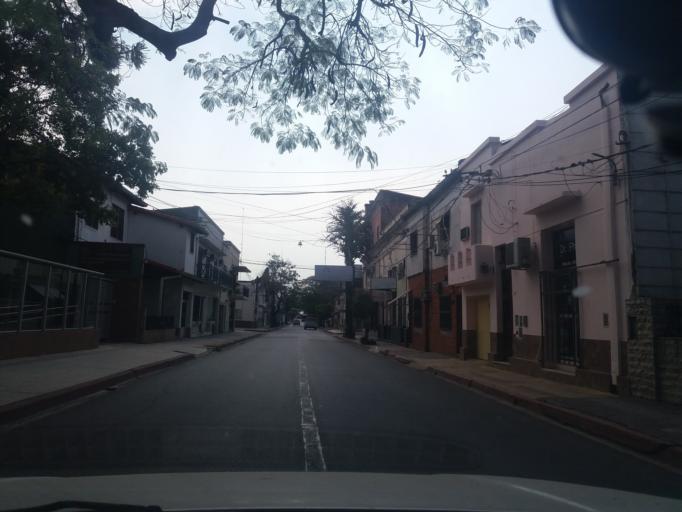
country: AR
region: Corrientes
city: Corrientes
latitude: -27.4713
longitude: -58.8385
